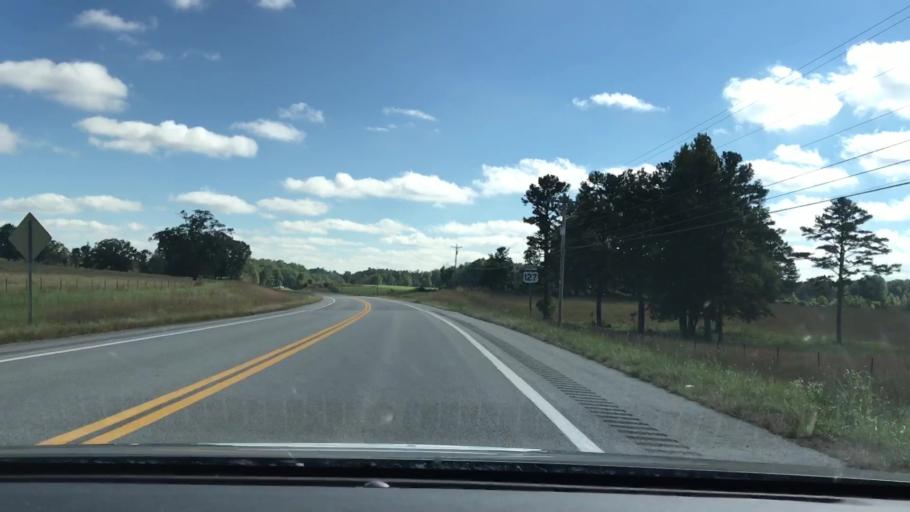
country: US
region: Tennessee
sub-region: Fentress County
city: Grimsley
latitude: 36.3060
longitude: -84.9750
